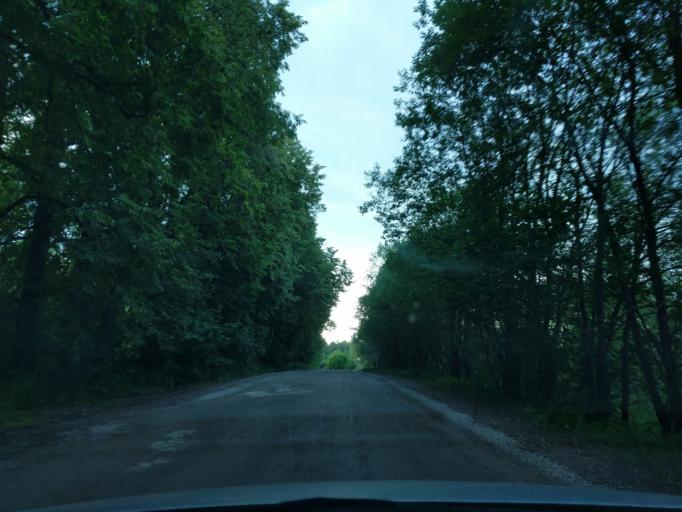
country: RU
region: Kaluga
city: Myatlevo
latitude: 54.8632
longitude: 35.5689
